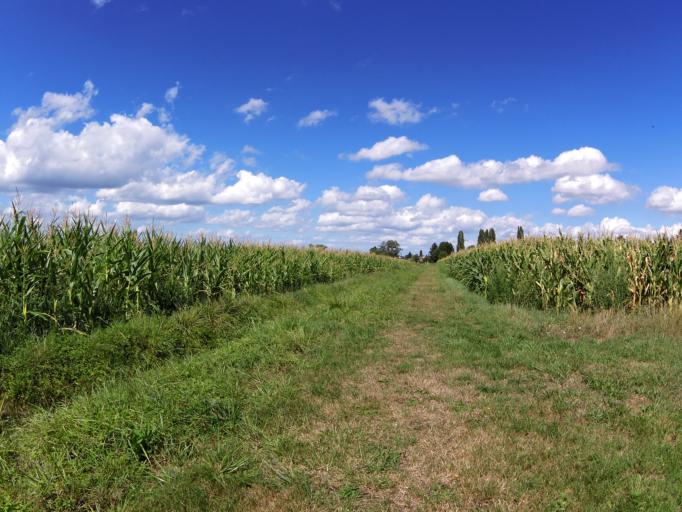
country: DE
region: Baden-Wuerttemberg
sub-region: Freiburg Region
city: Lahr
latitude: 48.3555
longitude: 7.8340
